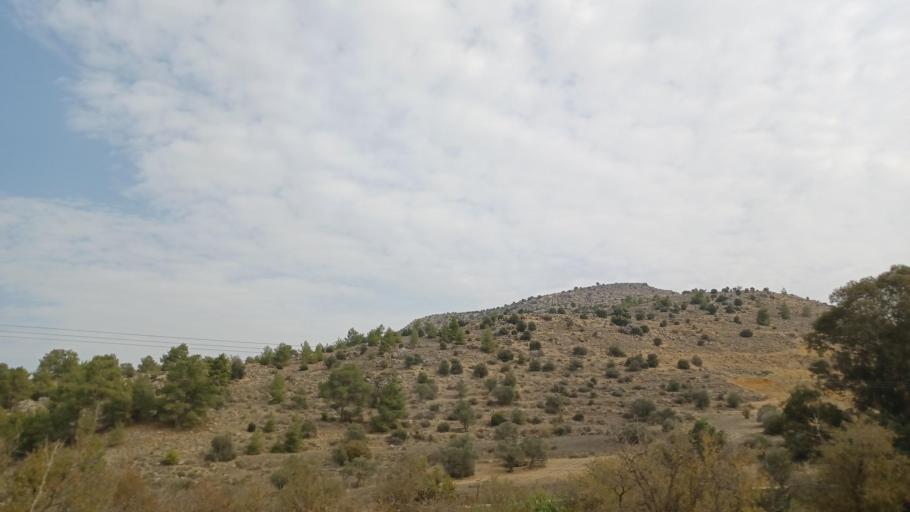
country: CY
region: Lefkosia
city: Klirou
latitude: 35.0493
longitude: 33.1251
